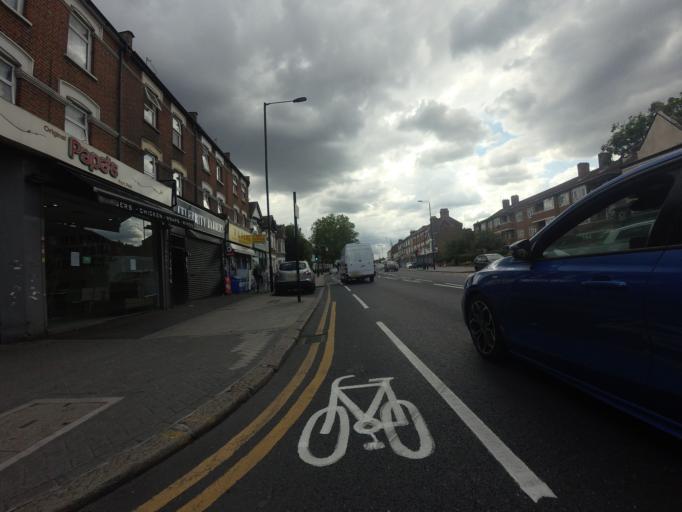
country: GB
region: England
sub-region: Greater London
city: Ilford
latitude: 51.5551
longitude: 0.0607
